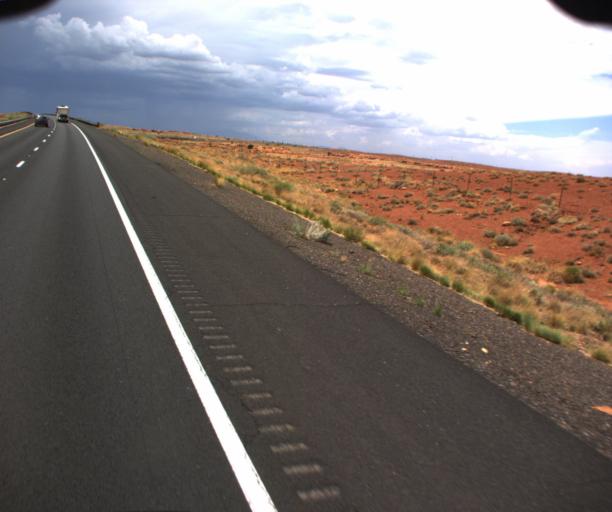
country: US
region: Arizona
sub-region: Coconino County
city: LeChee
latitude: 35.0998
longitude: -110.9676
